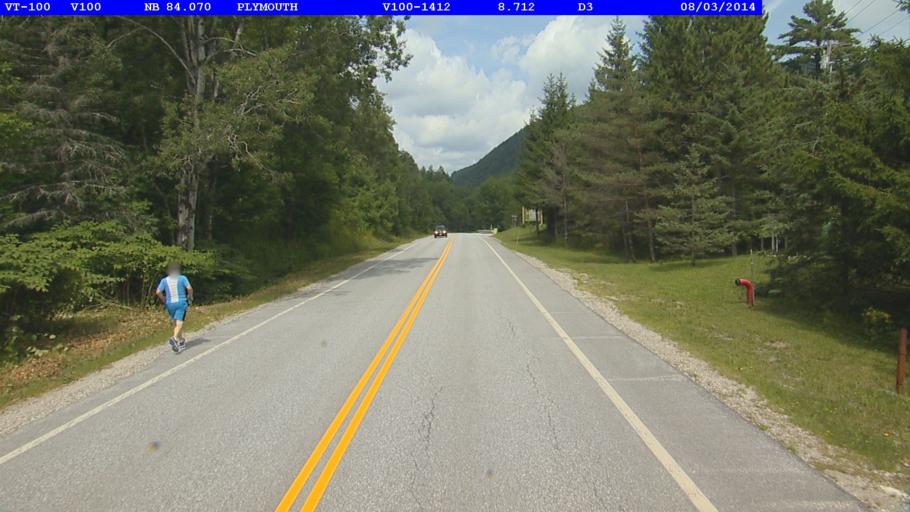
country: US
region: Vermont
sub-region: Rutland County
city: Rutland
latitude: 43.5738
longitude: -72.7621
